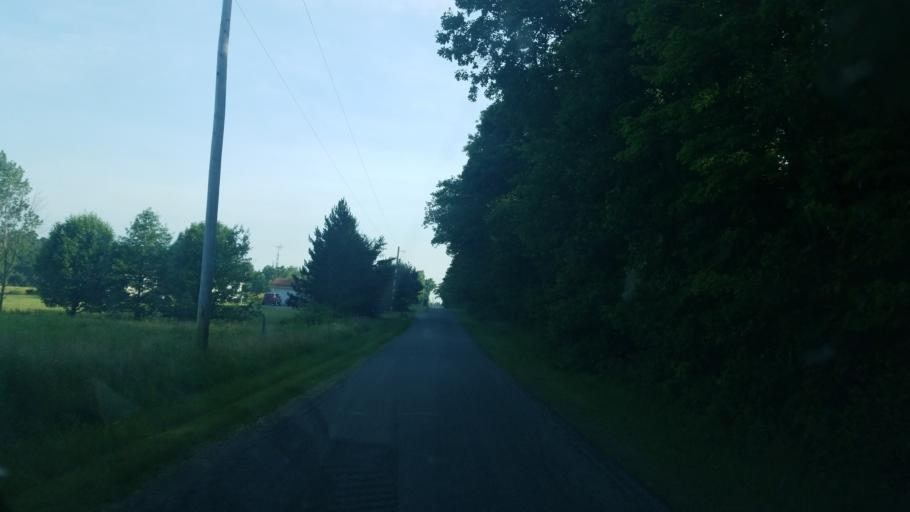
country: US
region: Ohio
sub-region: Hancock County
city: Arlington
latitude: 40.8371
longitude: -83.6704
